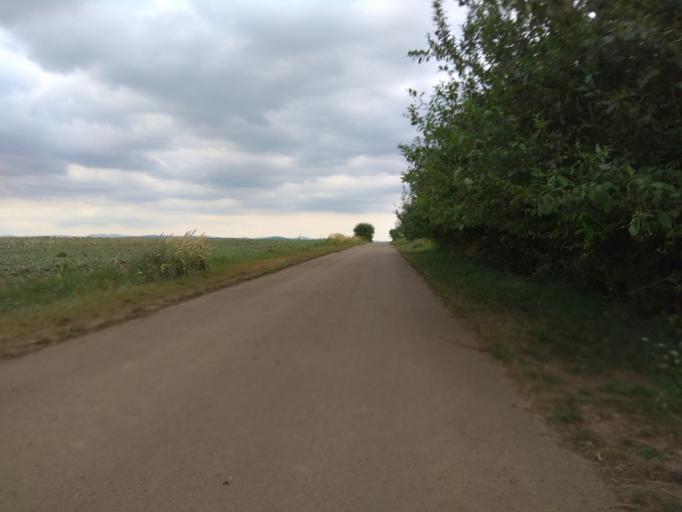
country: HU
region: Borsod-Abauj-Zemplen
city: Megyaszo
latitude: 48.1398
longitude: 21.0334
